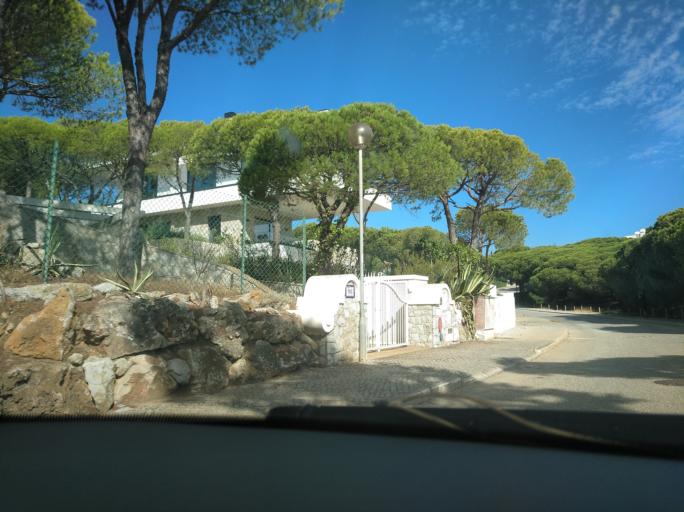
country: PT
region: Faro
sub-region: Vila Real de Santo Antonio
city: Monte Gordo
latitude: 37.1799
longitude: -7.4804
